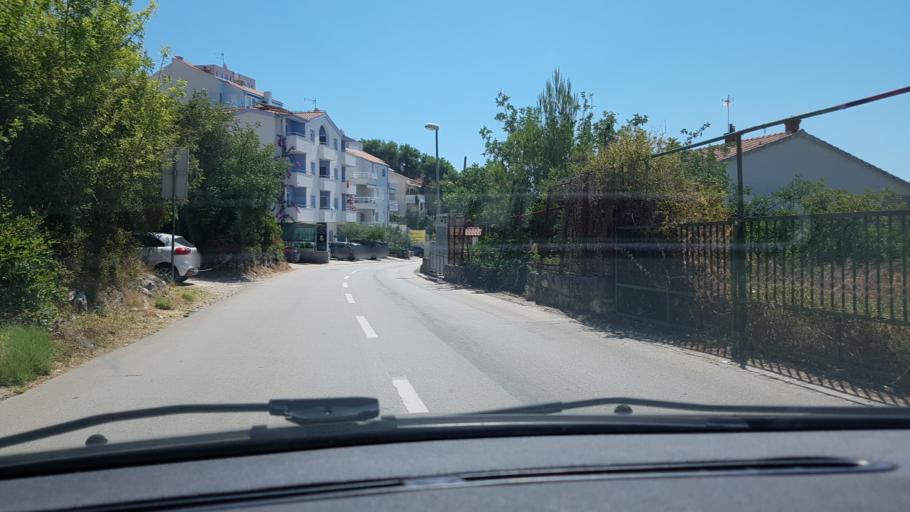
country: HR
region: Splitsko-Dalmatinska
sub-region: Grad Trogir
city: Trogir
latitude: 43.5098
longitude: 16.2554
